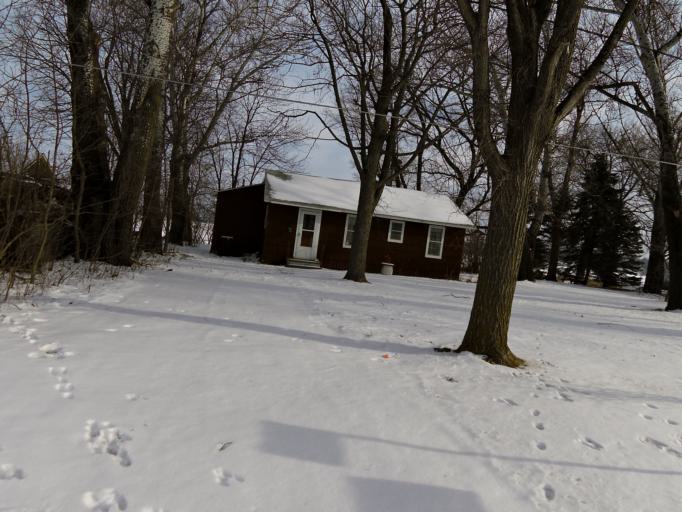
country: US
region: Minnesota
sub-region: Scott County
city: Prior Lake
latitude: 44.6986
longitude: -93.4884
